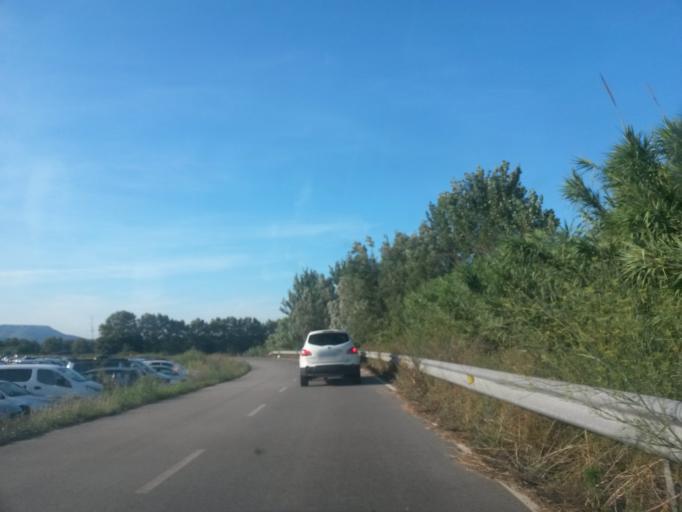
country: ES
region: Catalonia
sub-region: Provincia de Girona
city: Pals
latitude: 42.0003
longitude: 3.1692
